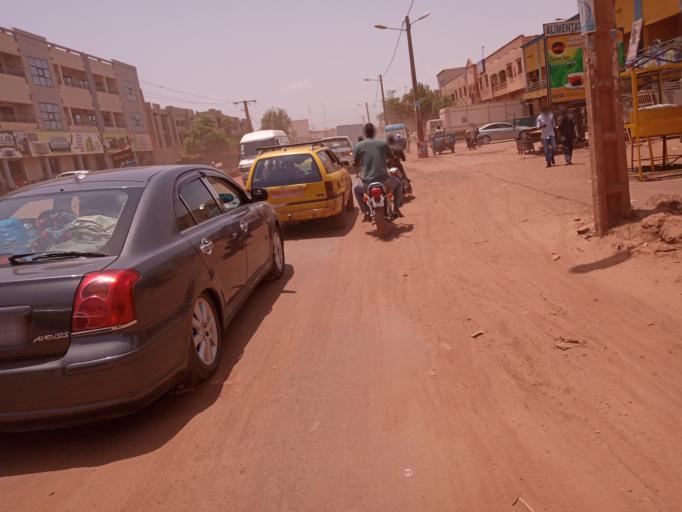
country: ML
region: Bamako
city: Bamako
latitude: 12.6513
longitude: -7.9538
